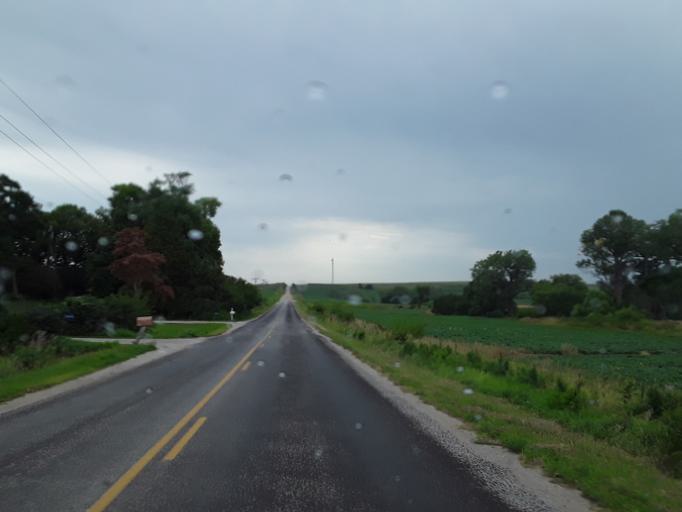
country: US
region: Nebraska
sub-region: Washington County
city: Blair
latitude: 41.5092
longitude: -96.1630
